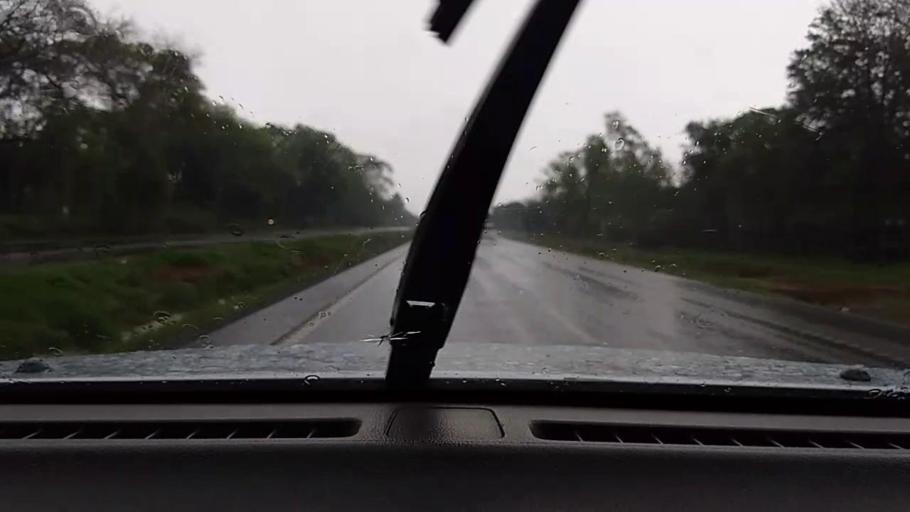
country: PY
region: Caaguazu
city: Repatriacion
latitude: -25.4500
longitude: -55.8988
